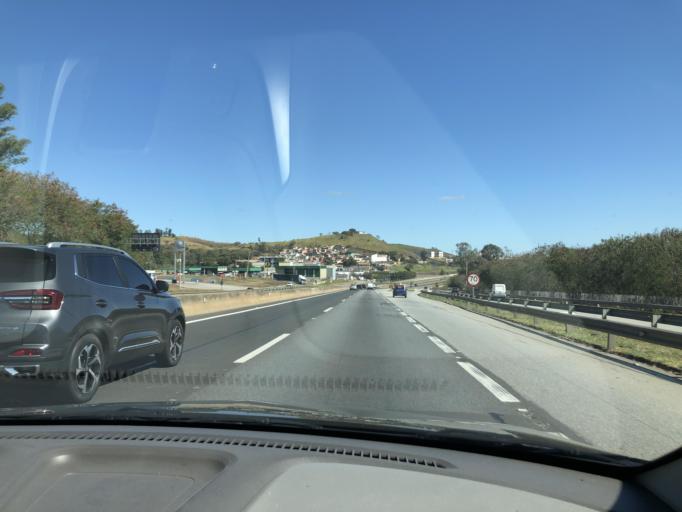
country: BR
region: Sao Paulo
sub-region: Sorocaba
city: Sorocaba
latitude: -23.5113
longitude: -47.4213
